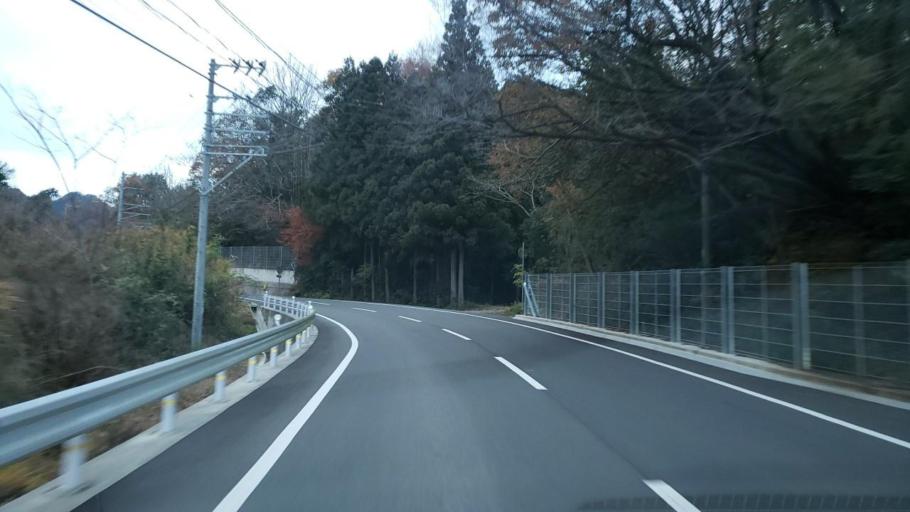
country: JP
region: Kagawa
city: Shido
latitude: 34.1971
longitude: 134.2506
